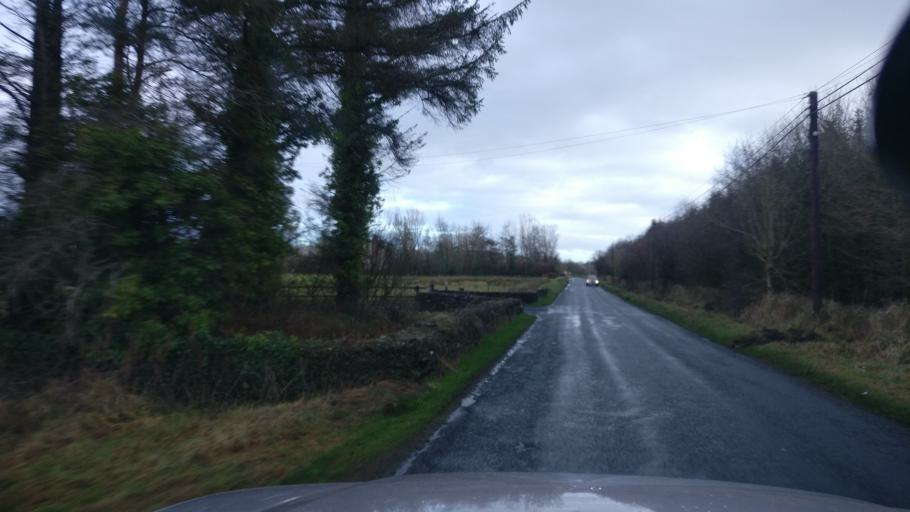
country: IE
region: Connaught
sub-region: County Galway
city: Athenry
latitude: 53.2971
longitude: -8.7031
